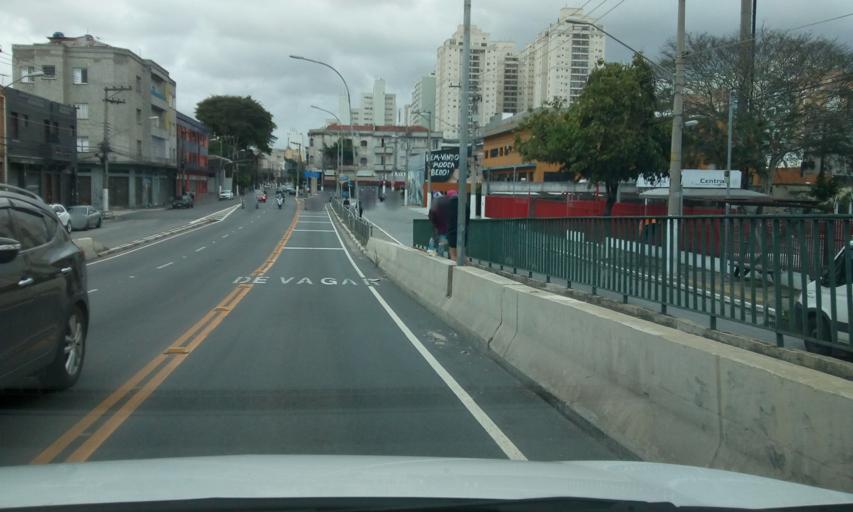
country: BR
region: Sao Paulo
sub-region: Sao Paulo
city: Sao Paulo
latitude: -23.5548
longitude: -46.6088
